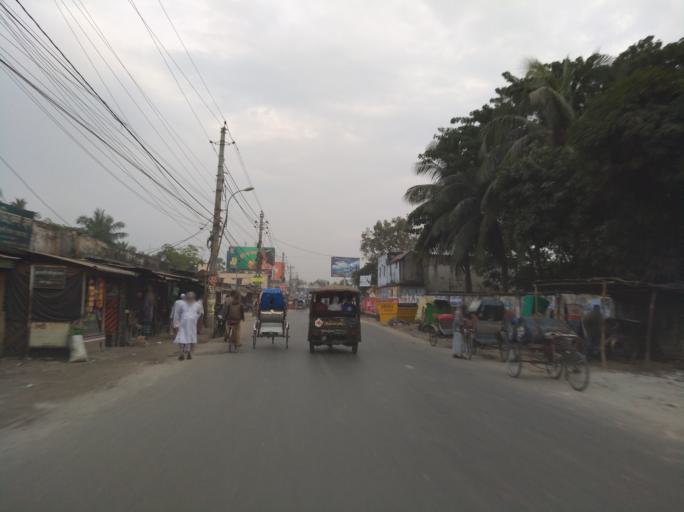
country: BD
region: Khulna
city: Khulna
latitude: 22.8298
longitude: 89.5494
